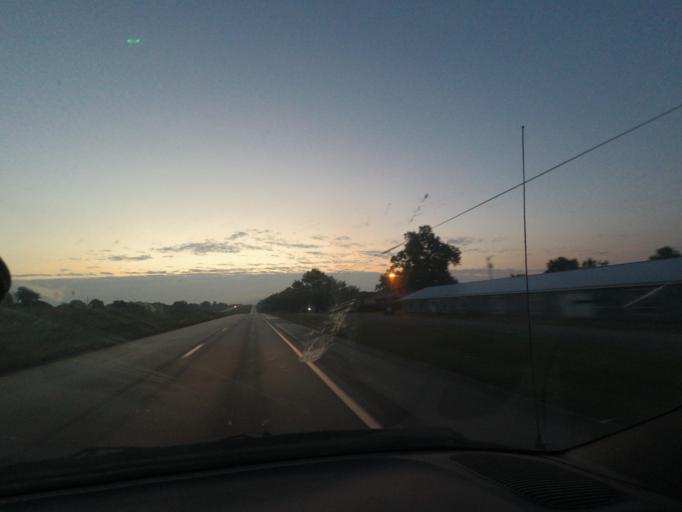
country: US
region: Missouri
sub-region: Linn County
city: Brookfield
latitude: 39.7793
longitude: -93.1277
